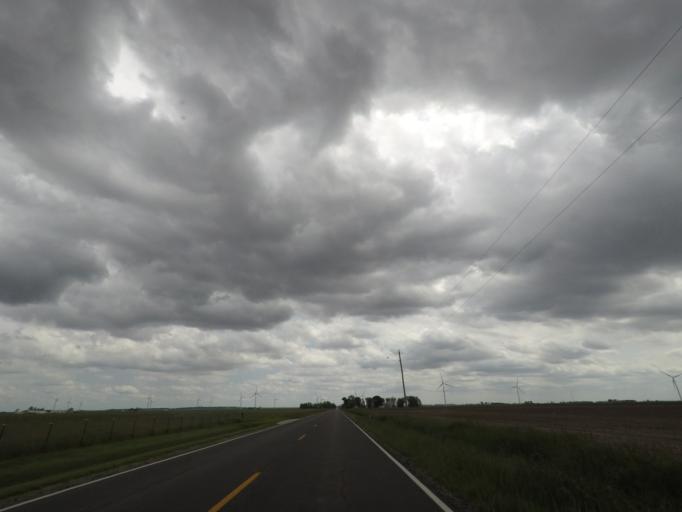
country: US
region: Illinois
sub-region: Macon County
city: Warrensburg
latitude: 39.9856
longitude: -89.0857
